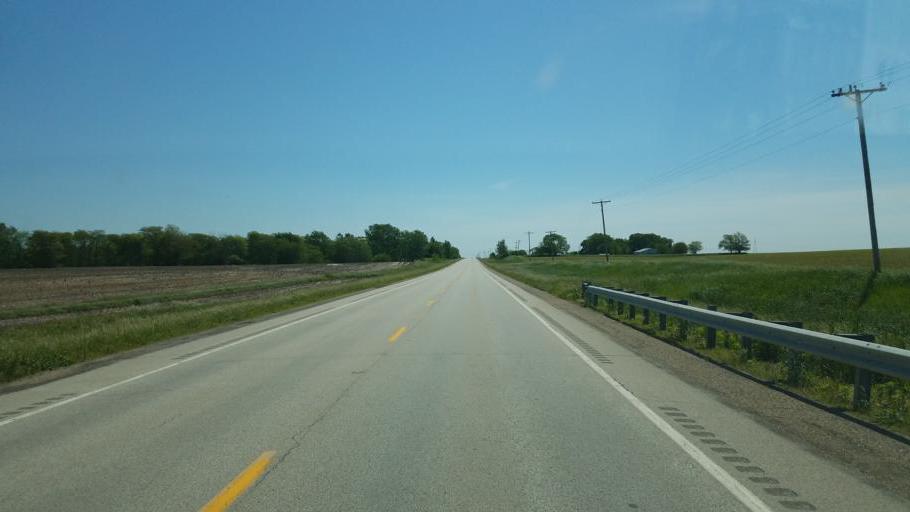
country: US
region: Illinois
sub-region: McLean County
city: Heyworth
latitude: 40.3122
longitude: -88.9561
